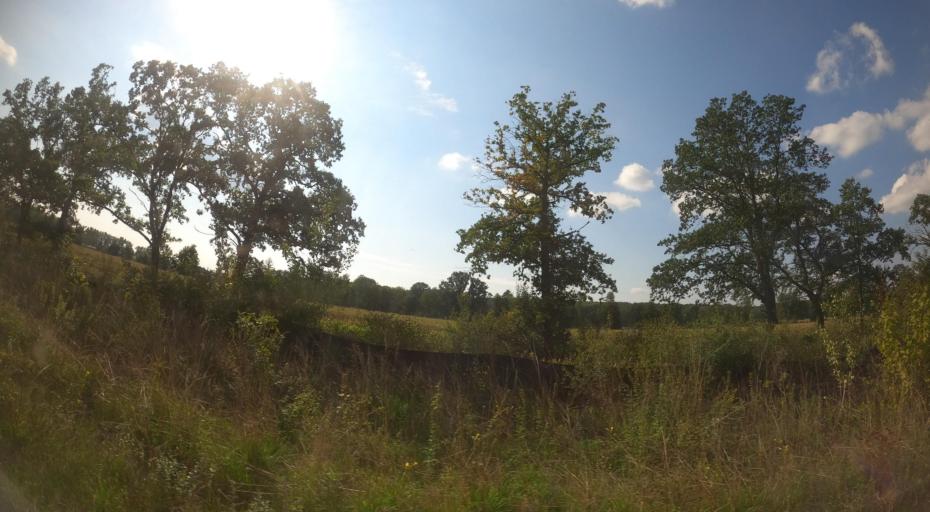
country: PL
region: Lubusz
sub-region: Powiat zielonogorski
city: Swidnica
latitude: 51.8916
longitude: 15.3167
